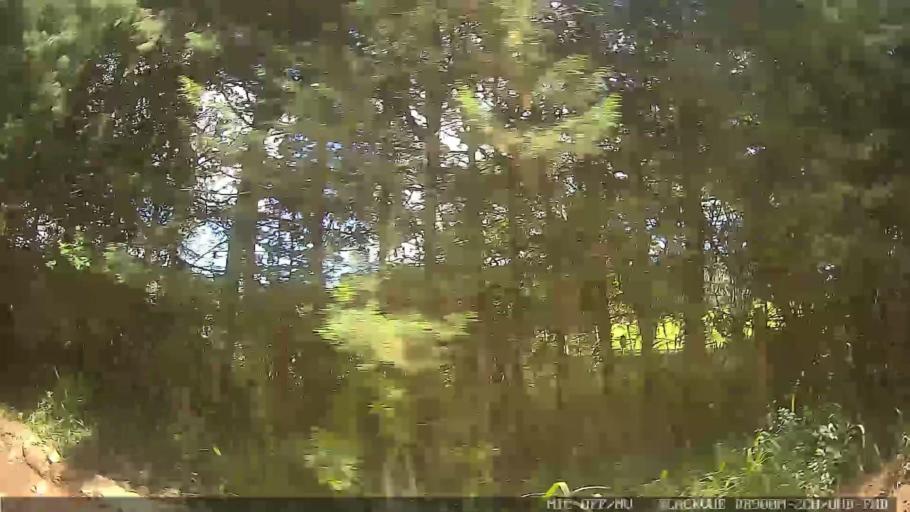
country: BR
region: Sao Paulo
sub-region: Bom Jesus Dos Perdoes
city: Bom Jesus dos Perdoes
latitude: -23.1340
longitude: -46.5034
